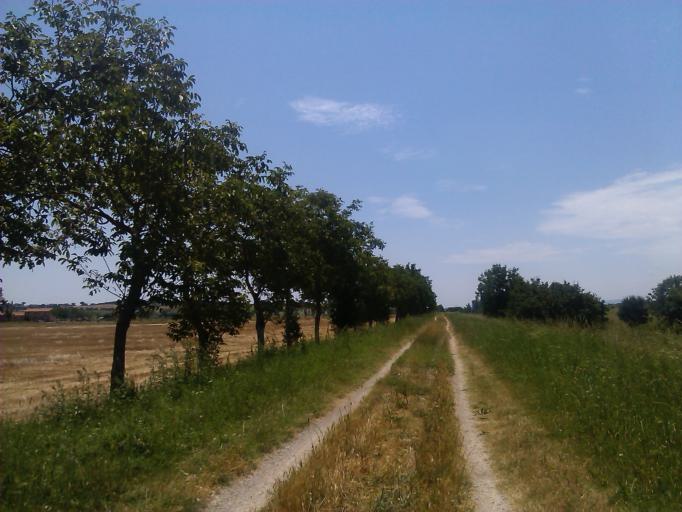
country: IT
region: Tuscany
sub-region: Province of Arezzo
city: Cesa
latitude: 43.3074
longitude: 11.8392
